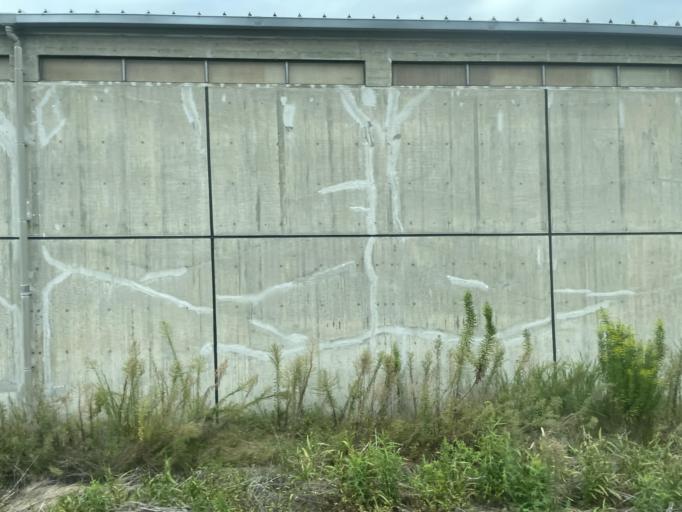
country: JP
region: Osaka
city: Kishiwada
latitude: 34.4619
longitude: 135.4014
